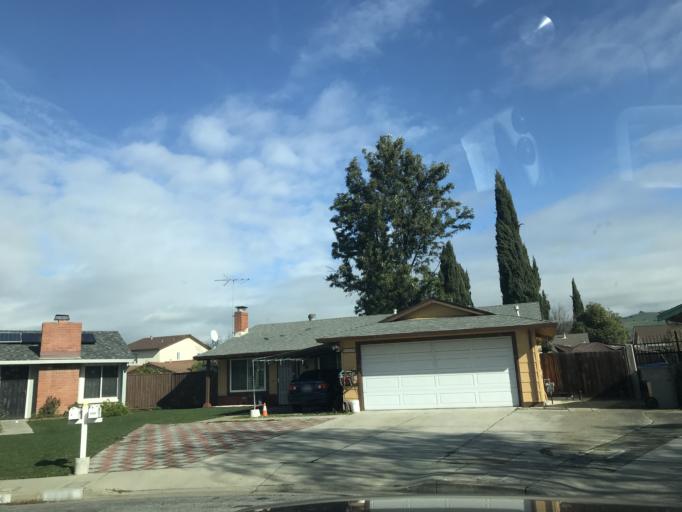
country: US
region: California
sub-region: Santa Clara County
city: Alum Rock
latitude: 37.3907
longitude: -121.8679
